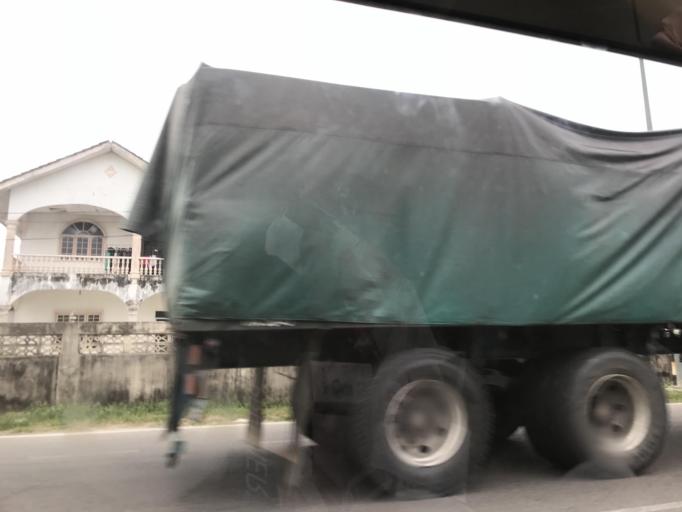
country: MY
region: Kelantan
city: Kota Bharu
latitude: 6.1388
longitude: 102.2176
